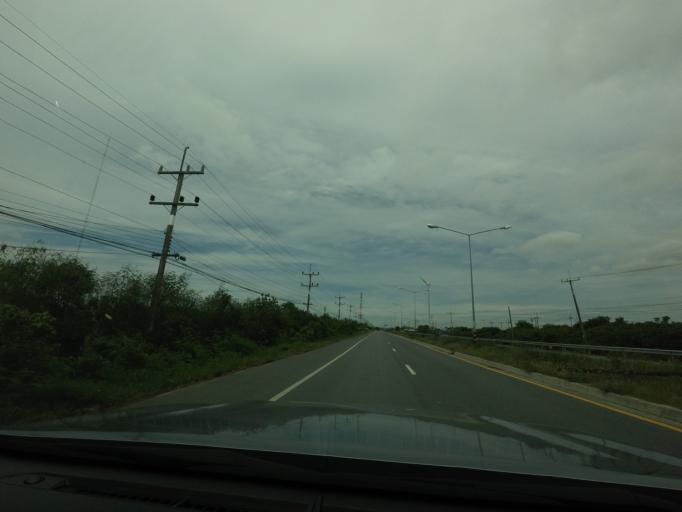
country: TH
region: Songkhla
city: Ranot
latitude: 7.8976
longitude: 100.3407
